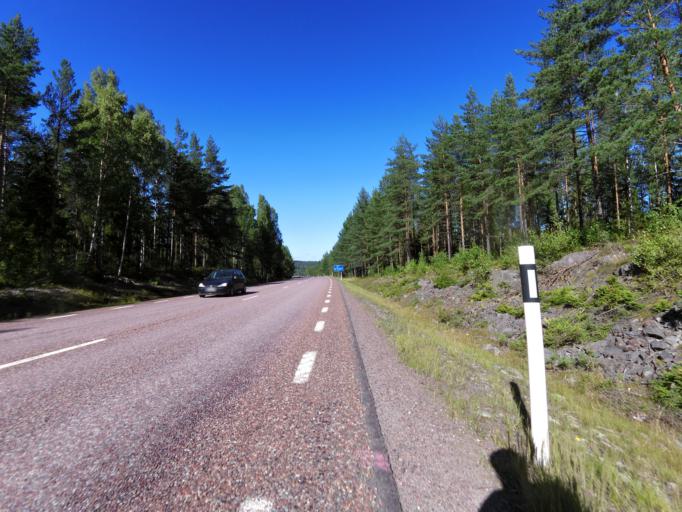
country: SE
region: Gaevleborg
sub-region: Sandvikens Kommun
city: Jarbo
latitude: 60.5606
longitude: 16.4854
